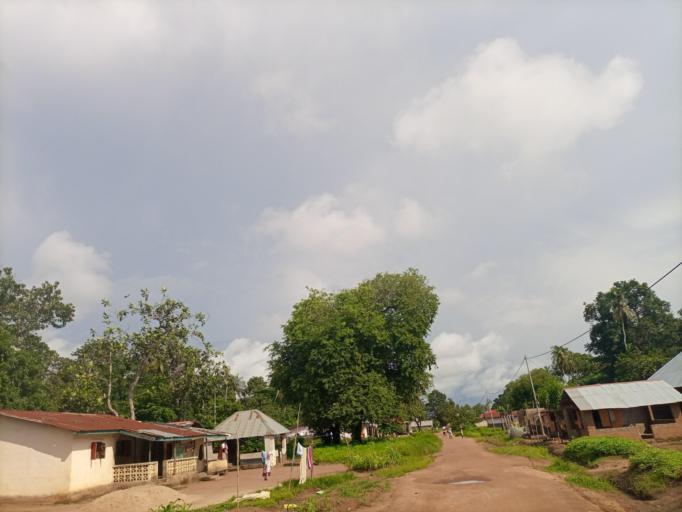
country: SL
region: Northern Province
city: Masoyila
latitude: 8.6188
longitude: -13.1718
